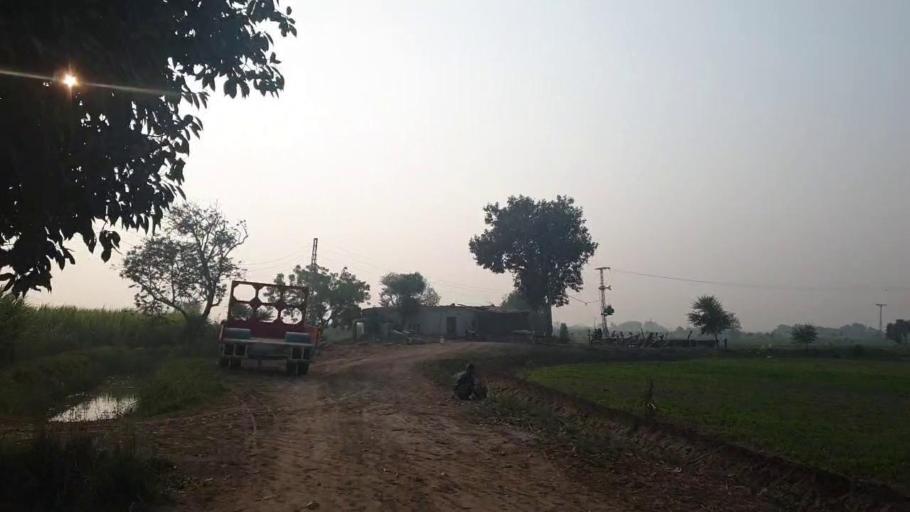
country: PK
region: Sindh
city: Hyderabad
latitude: 25.3226
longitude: 68.4732
